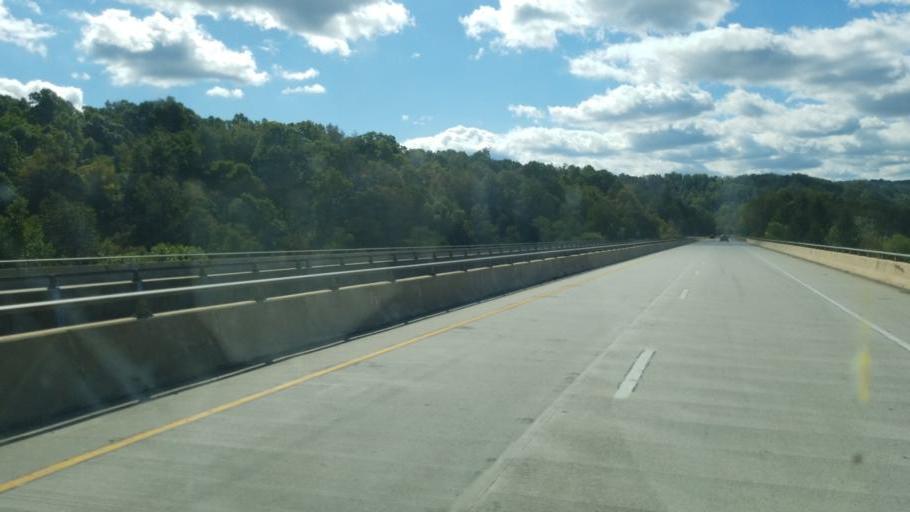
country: US
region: Maryland
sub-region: Garrett County
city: Oakland
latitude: 39.6621
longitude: -79.3973
